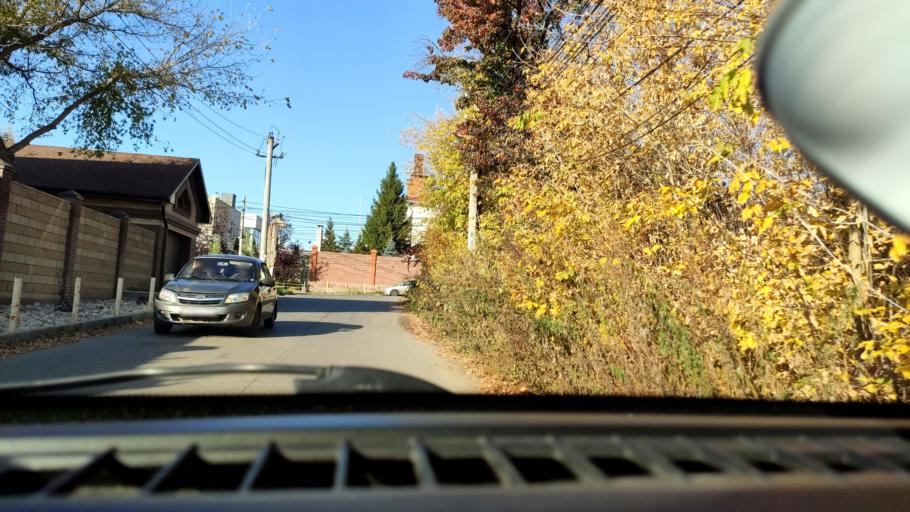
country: RU
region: Samara
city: Samara
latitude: 53.2676
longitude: 50.1937
